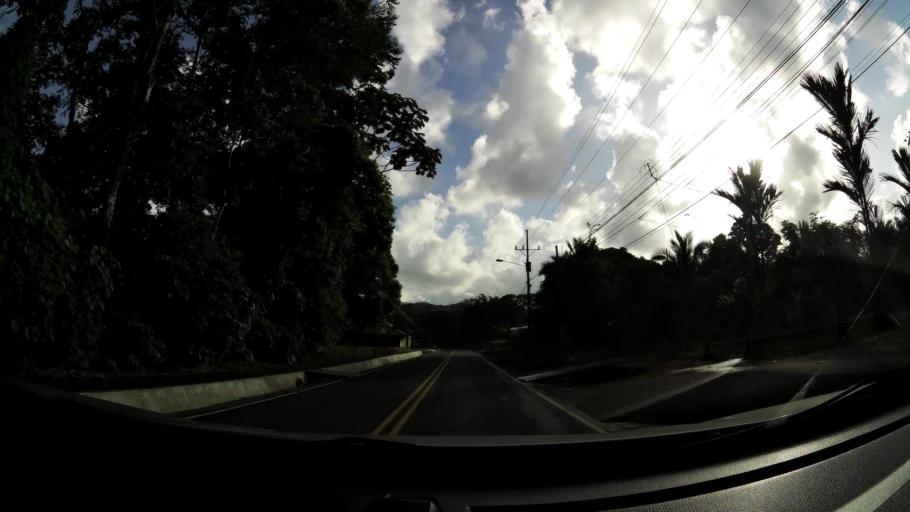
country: CR
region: Limon
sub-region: Canton de Siquirres
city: Siquirres
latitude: 10.0855
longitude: -83.5457
